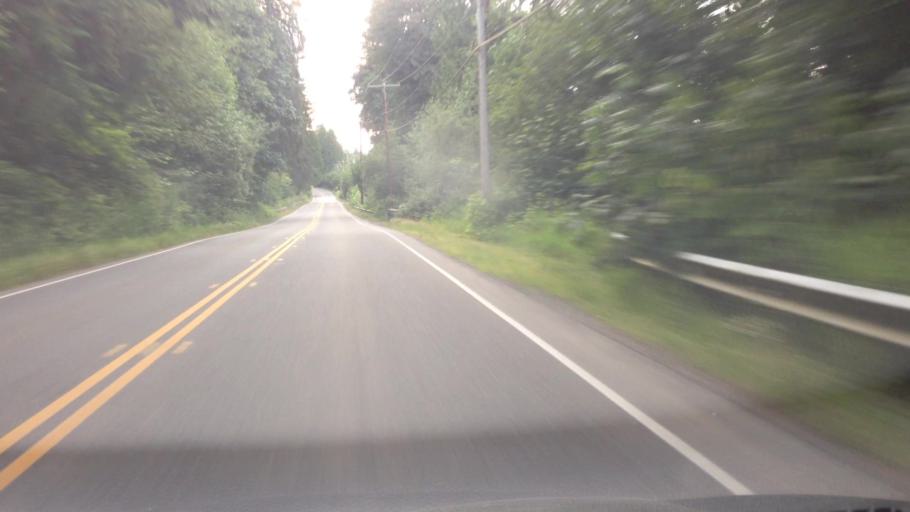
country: US
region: Washington
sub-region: King County
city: Duvall
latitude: 47.7449
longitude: -121.9529
